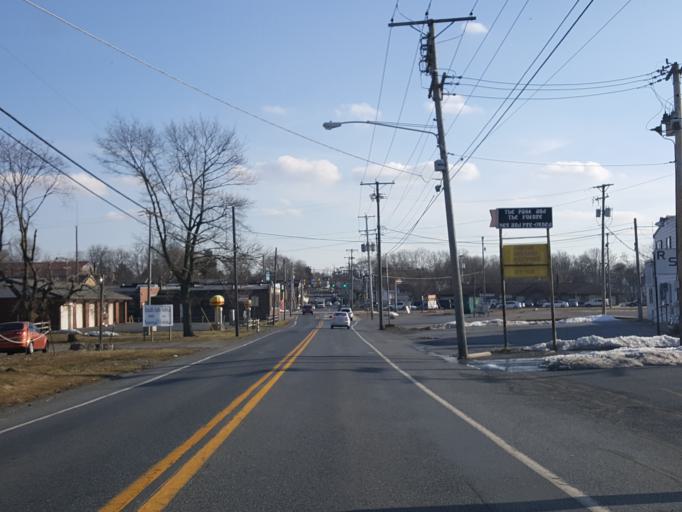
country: US
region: Pennsylvania
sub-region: Lebanon County
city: Pleasant Hill
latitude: 40.3399
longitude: -76.4399
